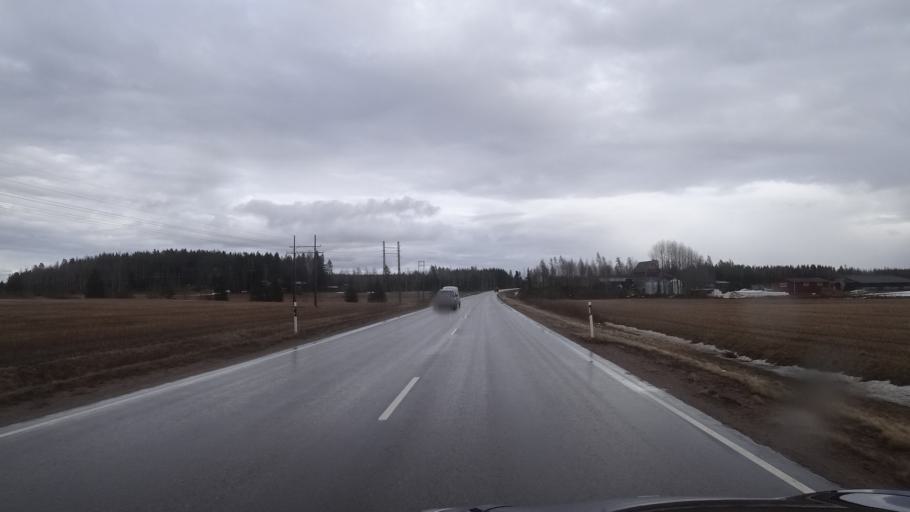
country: FI
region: Kymenlaakso
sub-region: Kouvola
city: Elimaeki
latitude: 60.7126
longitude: 26.4620
